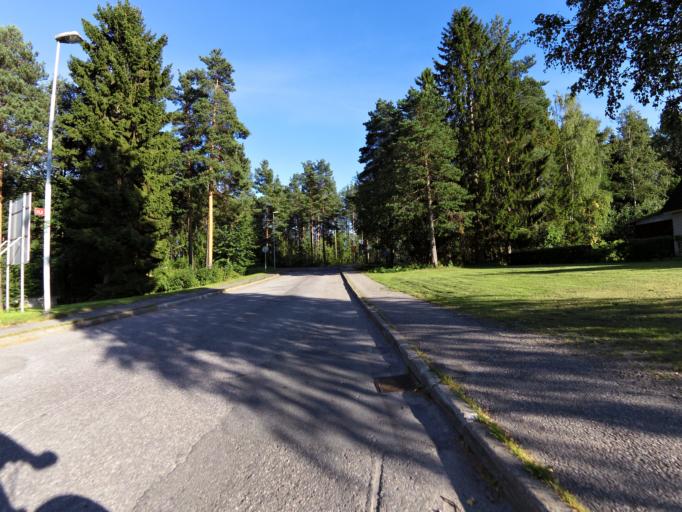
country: SE
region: Gaevleborg
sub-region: Gavle Kommun
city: Gavle
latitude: 60.6476
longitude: 17.1431
